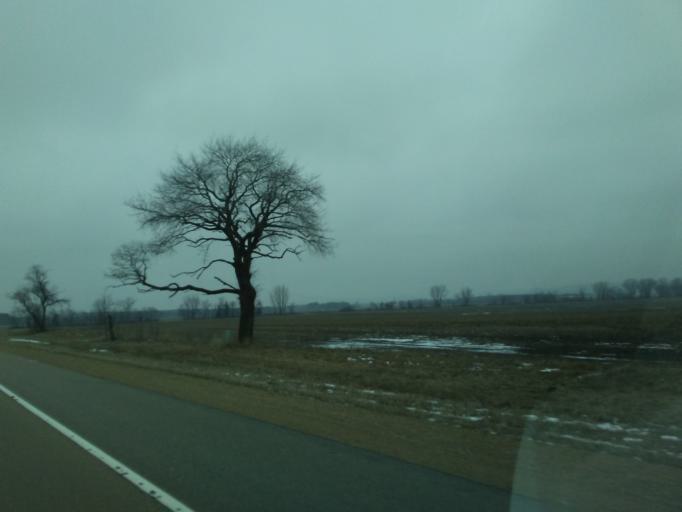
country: US
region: Wisconsin
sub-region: Sauk County
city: Spring Green
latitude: 43.1616
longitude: -89.9700
